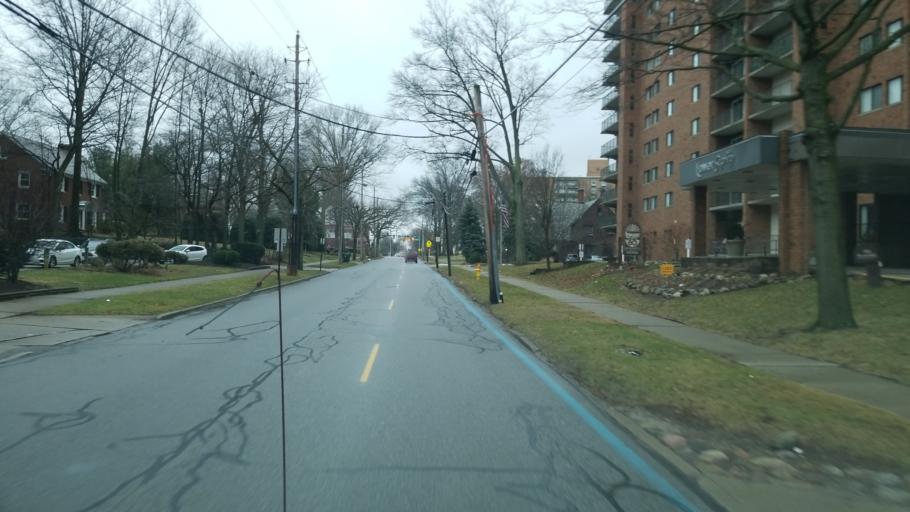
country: US
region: Ohio
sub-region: Summit County
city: Akron
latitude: 41.0995
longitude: -81.5460
